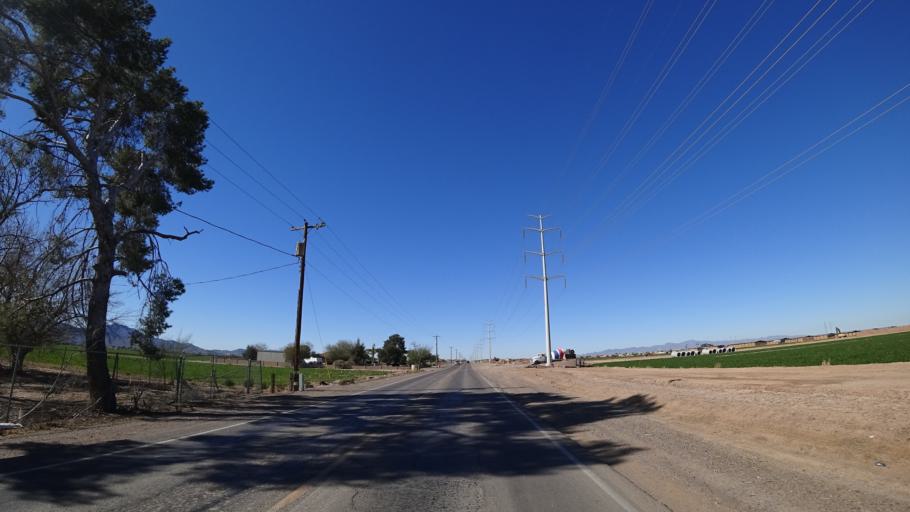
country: US
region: Arizona
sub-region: Maricopa County
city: Tolleson
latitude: 33.4065
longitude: -112.2626
